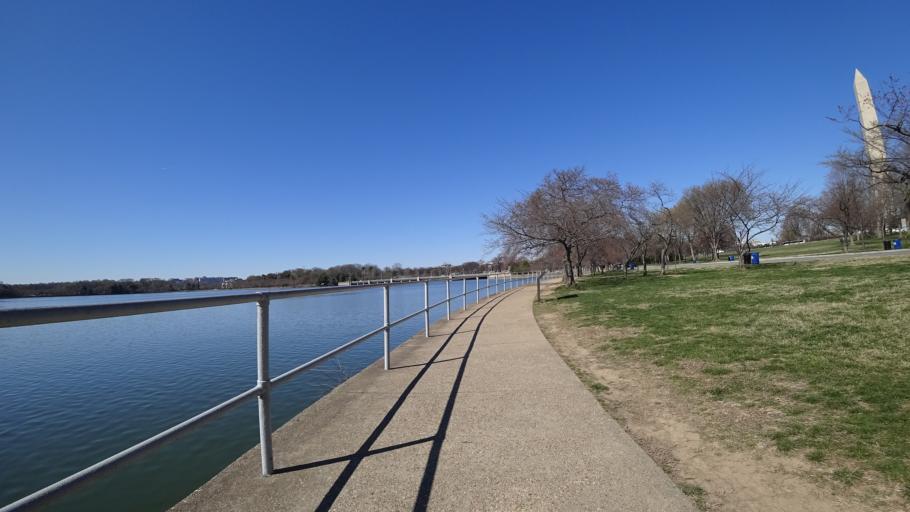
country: US
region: Washington, D.C.
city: Washington, D.C.
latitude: 38.8851
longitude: -77.0364
